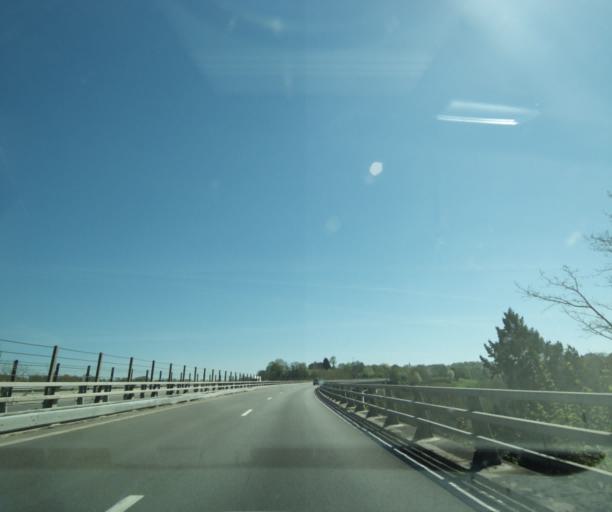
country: FR
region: Limousin
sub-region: Departement de la Haute-Vienne
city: Pierre-Buffiere
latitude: 45.6972
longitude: 1.3634
